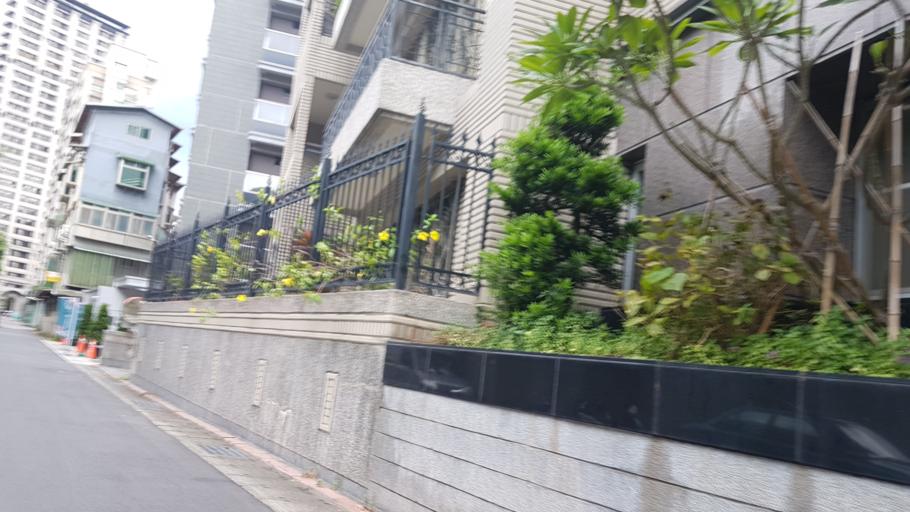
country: TW
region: Taipei
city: Taipei
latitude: 24.9914
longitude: 121.5684
